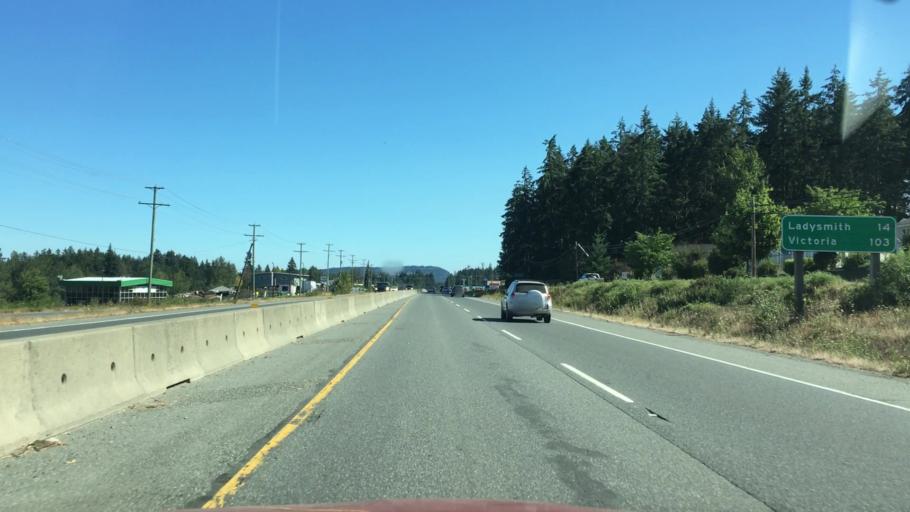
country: CA
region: British Columbia
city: Nanaimo
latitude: 49.1022
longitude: -123.8923
